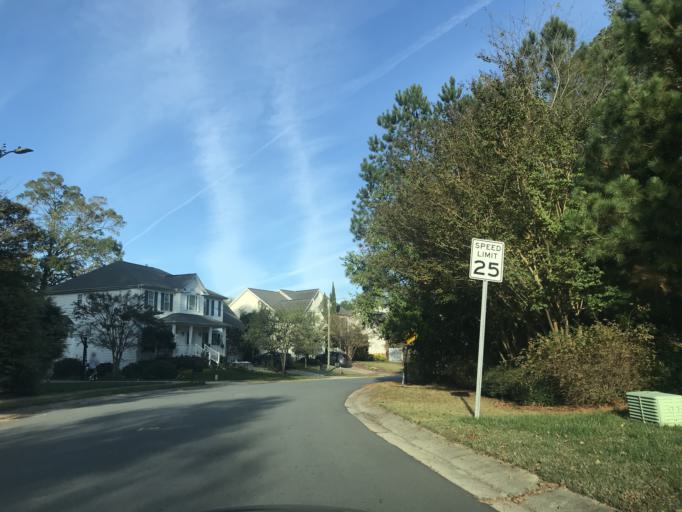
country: US
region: North Carolina
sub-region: Wake County
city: Rolesville
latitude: 35.8917
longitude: -78.5452
